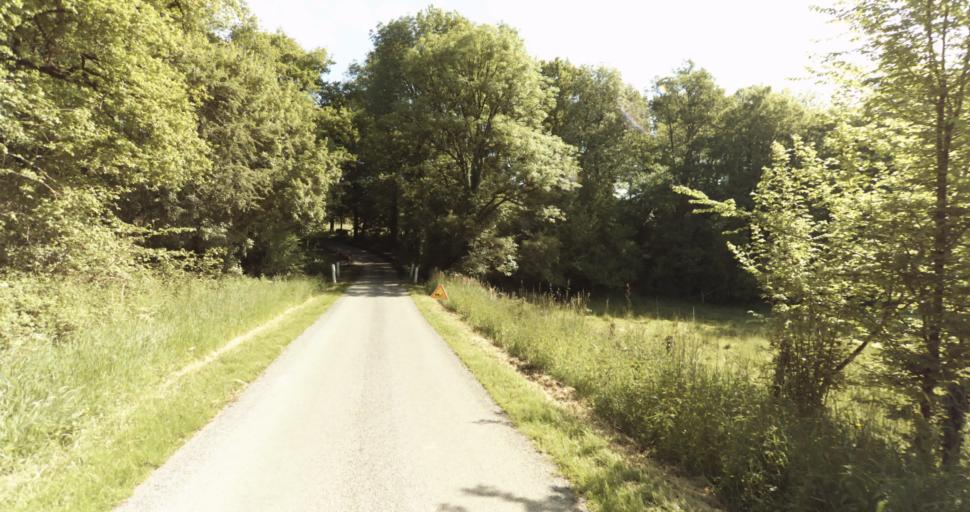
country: FR
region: Limousin
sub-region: Departement de la Haute-Vienne
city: Solignac
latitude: 45.6993
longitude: 1.2550
